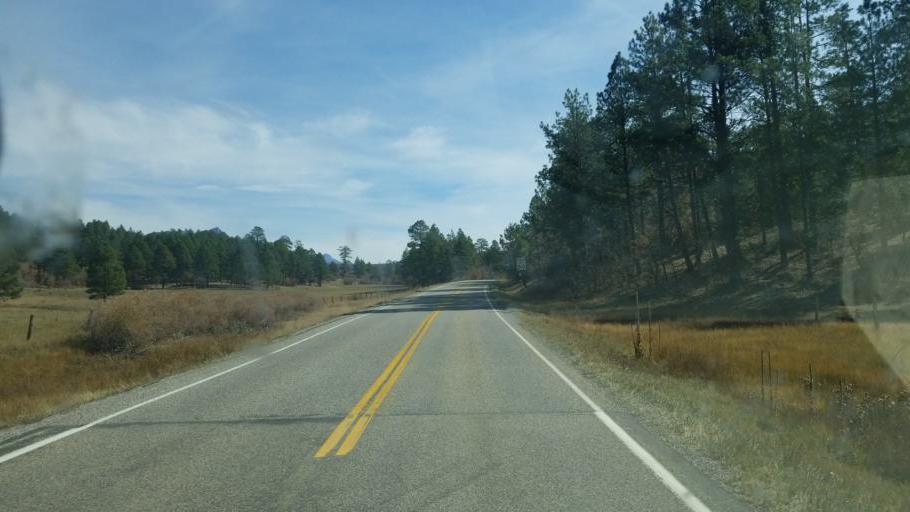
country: US
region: New Mexico
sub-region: Rio Arriba County
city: Dulce
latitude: 37.0750
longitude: -106.8391
